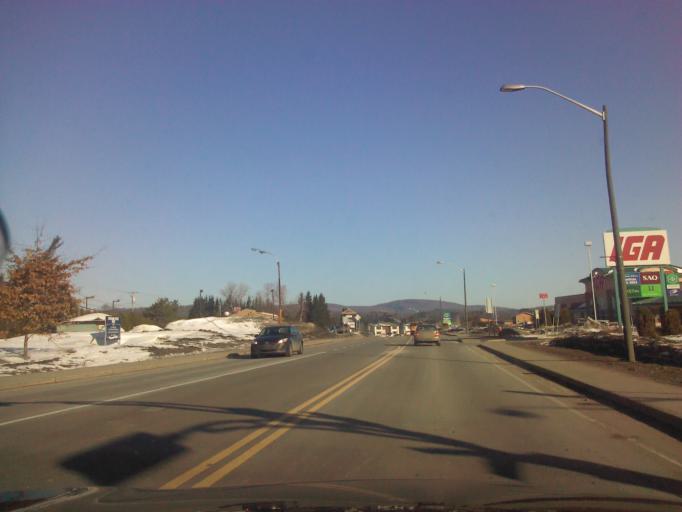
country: CA
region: Quebec
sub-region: Capitale-Nationale
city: Sainte Catherine de la Jacques Cartier
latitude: 46.8398
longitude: -71.6093
